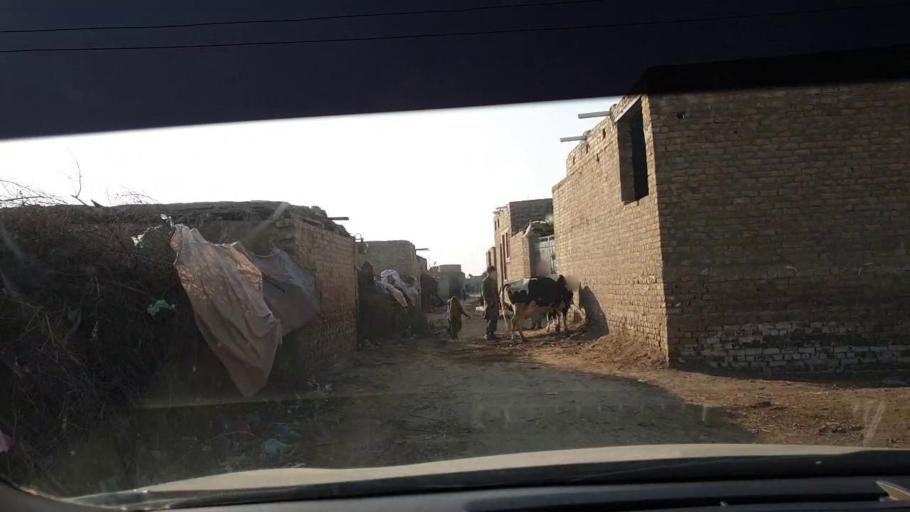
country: PK
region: Sindh
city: Berani
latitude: 25.8454
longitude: 68.7774
